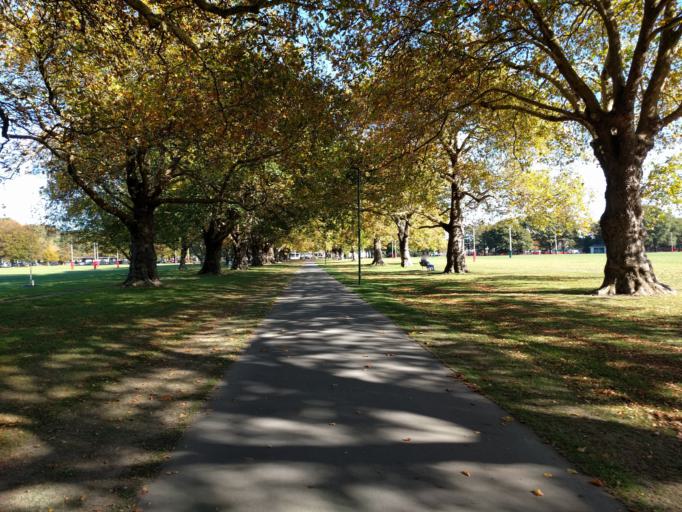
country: NZ
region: Canterbury
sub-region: Christchurch City
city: Christchurch
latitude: -43.5279
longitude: 172.6159
